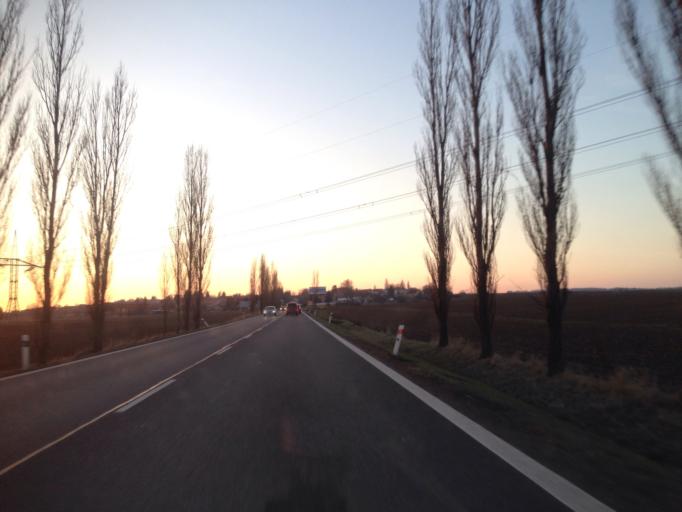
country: CZ
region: Central Bohemia
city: Revnicov
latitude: 50.1778
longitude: 13.8183
